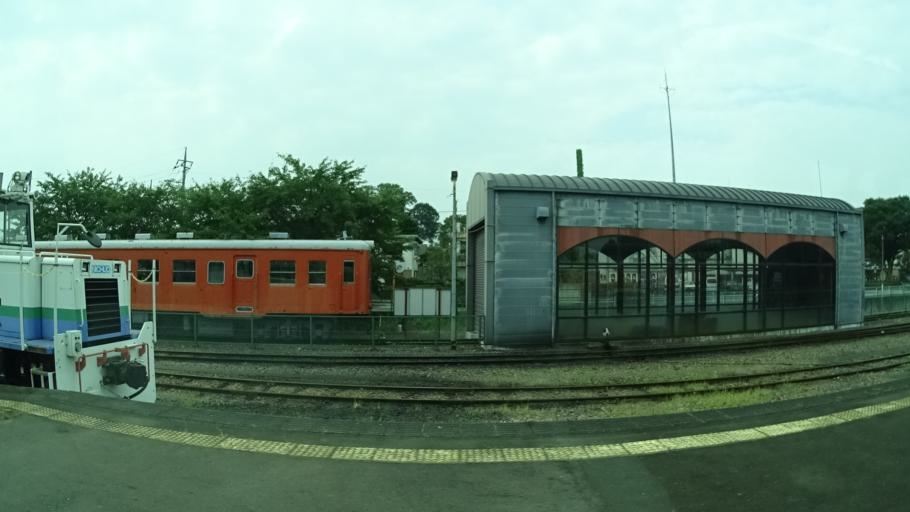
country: JP
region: Tochigi
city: Mooka
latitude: 36.4388
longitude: 140.0025
